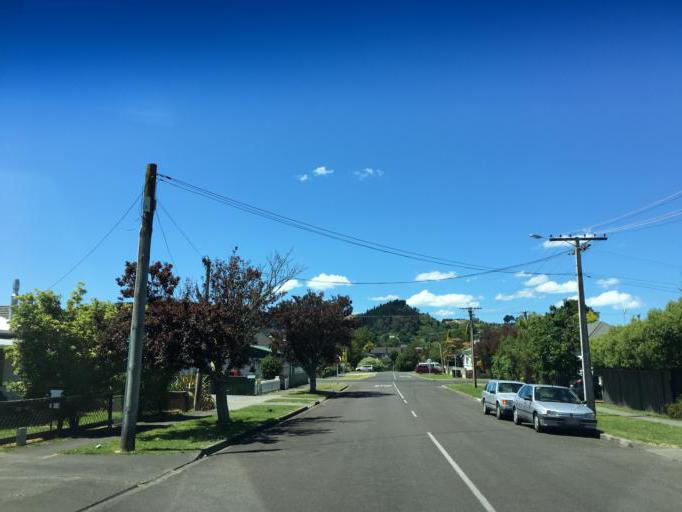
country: NZ
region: Gisborne
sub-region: Gisborne District
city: Gisborne
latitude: -38.6604
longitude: 178.0237
